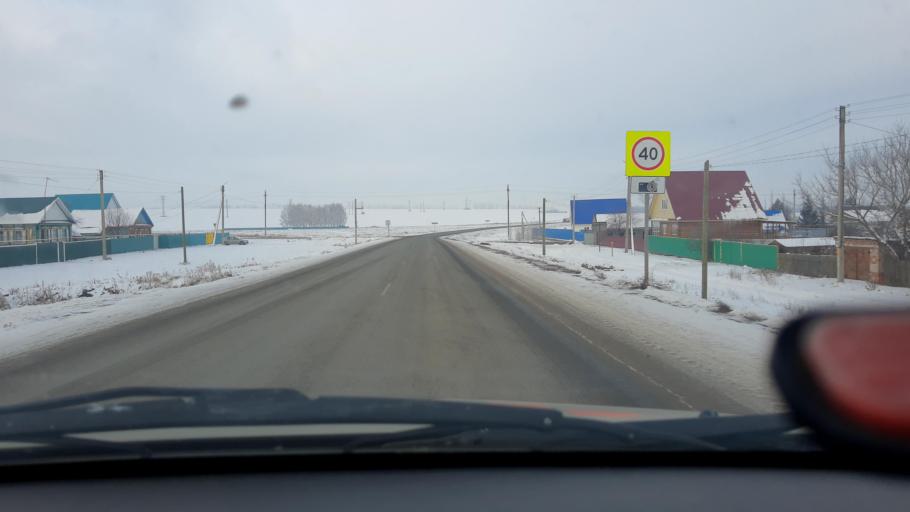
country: RU
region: Bashkortostan
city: Avdon
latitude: 54.3822
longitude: 55.8068
